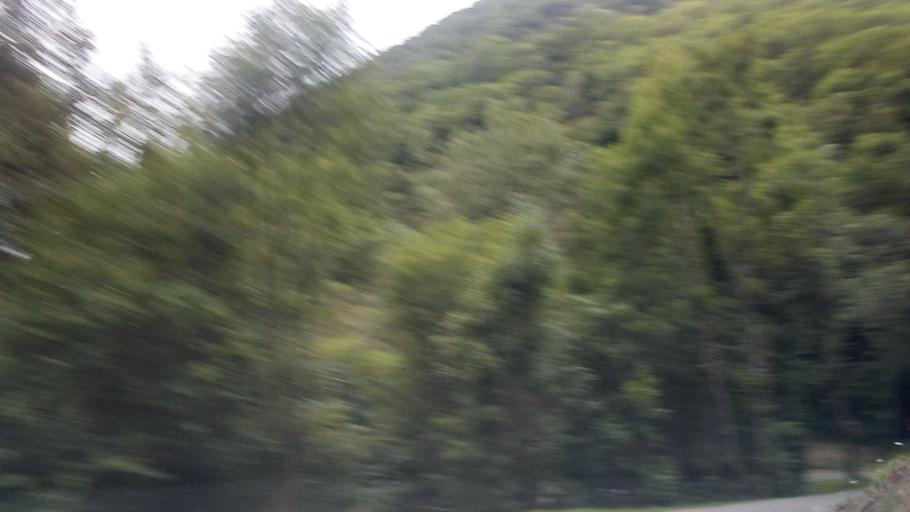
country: FR
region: Midi-Pyrenees
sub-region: Departement des Hautes-Pyrenees
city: Saint-Lary-Soulan
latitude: 42.8656
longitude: 0.3315
